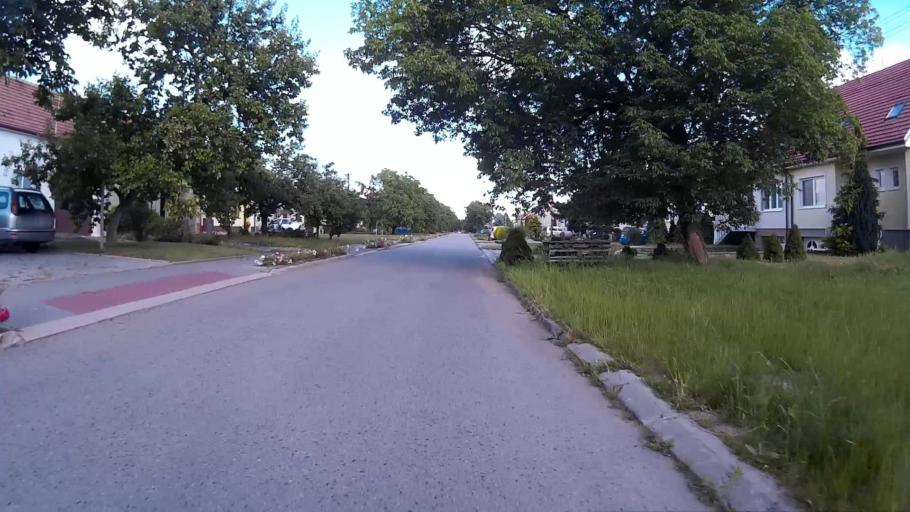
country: CZ
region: South Moravian
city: Tesany
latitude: 49.0438
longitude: 16.7682
